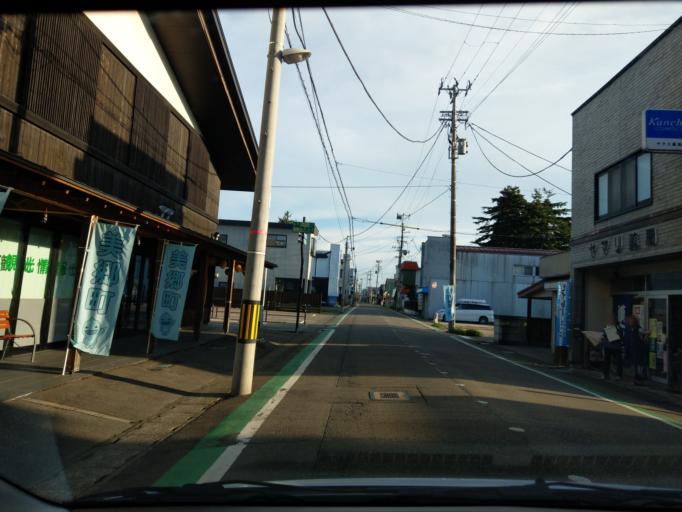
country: JP
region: Akita
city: Omagari
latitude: 39.4232
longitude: 140.5482
